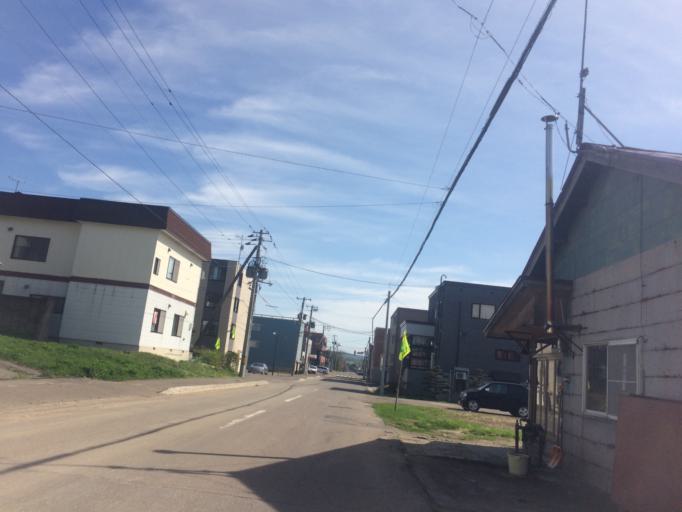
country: JP
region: Hokkaido
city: Niseko Town
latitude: 42.9051
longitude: 140.7561
